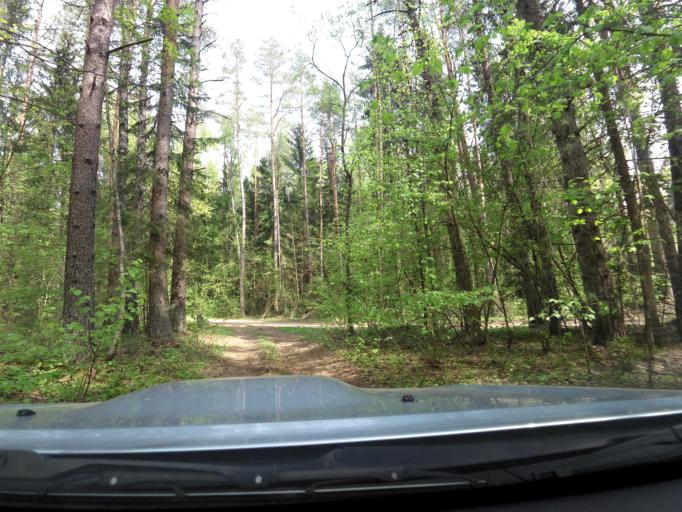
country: LT
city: Salcininkai
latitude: 54.4250
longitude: 25.3075
